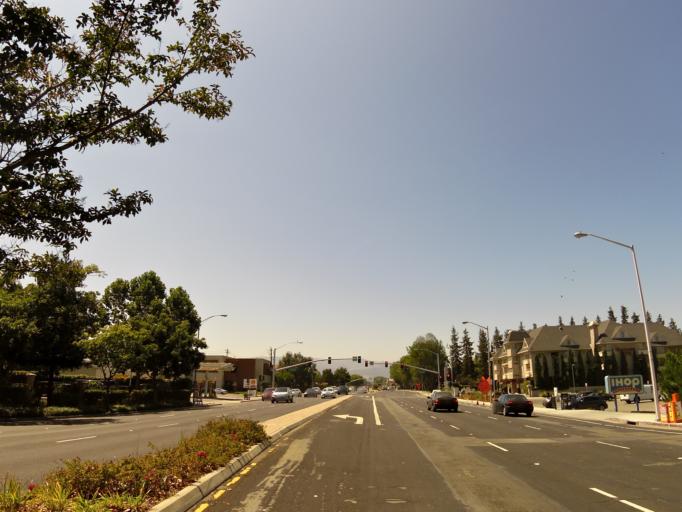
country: US
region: California
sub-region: Santa Clara County
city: Cupertino
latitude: 37.3230
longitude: -122.0021
